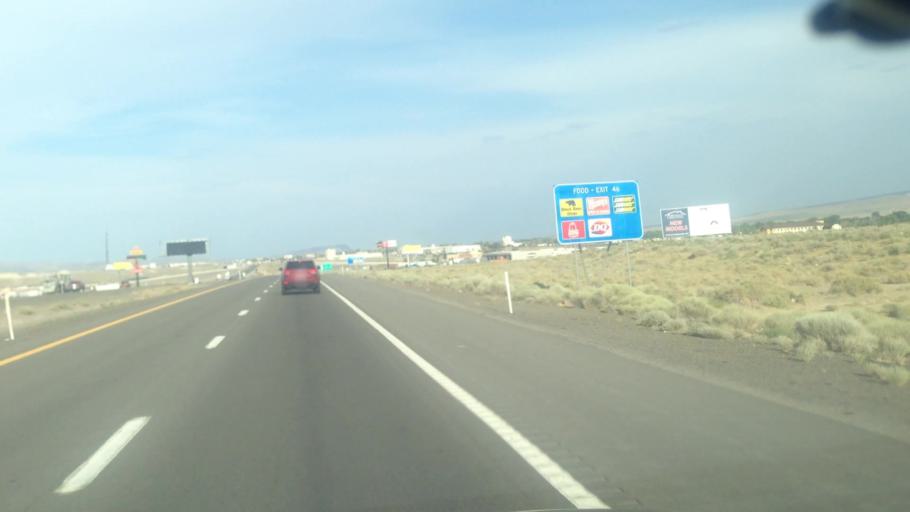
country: US
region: Nevada
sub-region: Lyon County
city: Fernley
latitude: 39.6173
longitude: -119.2760
